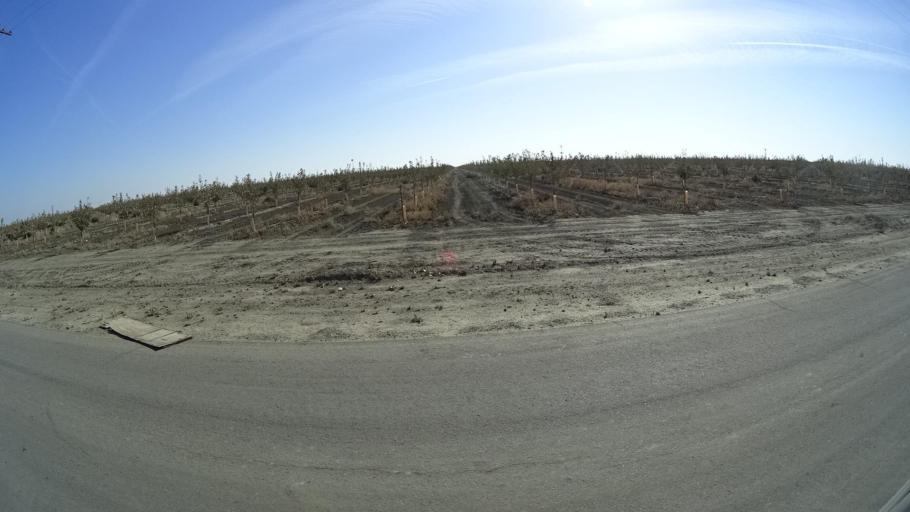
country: US
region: California
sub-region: Kern County
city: Wasco
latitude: 35.7031
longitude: -119.4230
